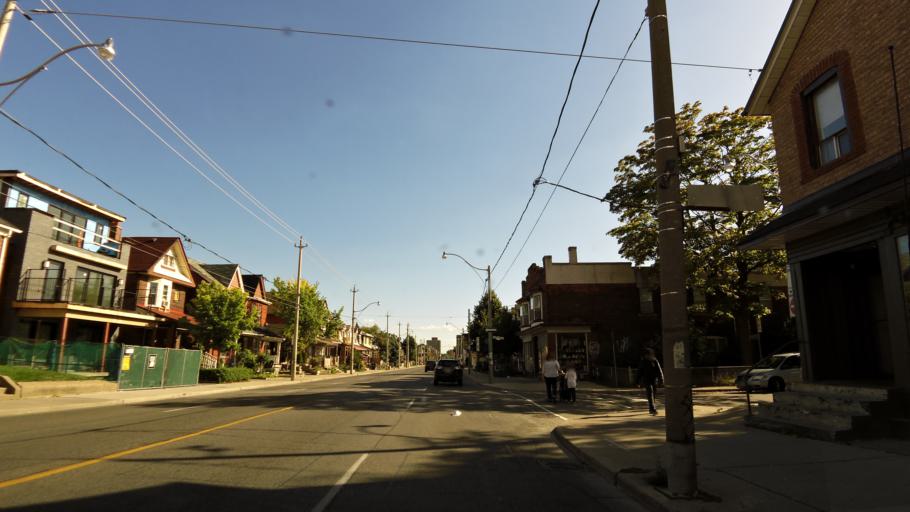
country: CA
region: Ontario
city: Toronto
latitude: 43.6649
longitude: -79.4376
